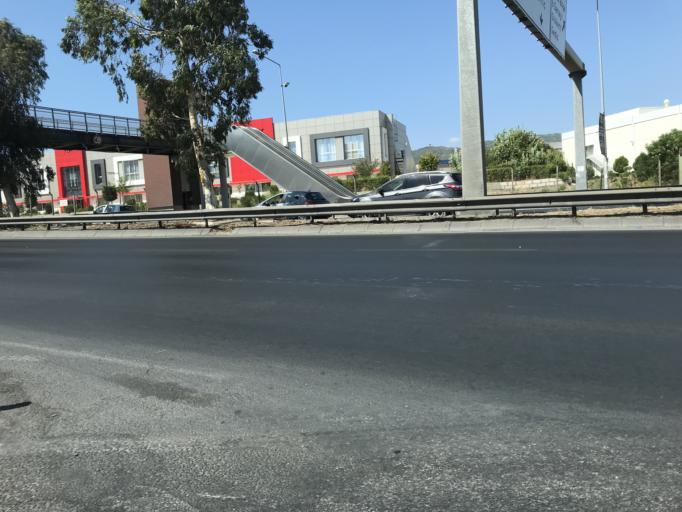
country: TR
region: Izmir
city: Gaziemir
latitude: 38.3408
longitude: 27.1335
